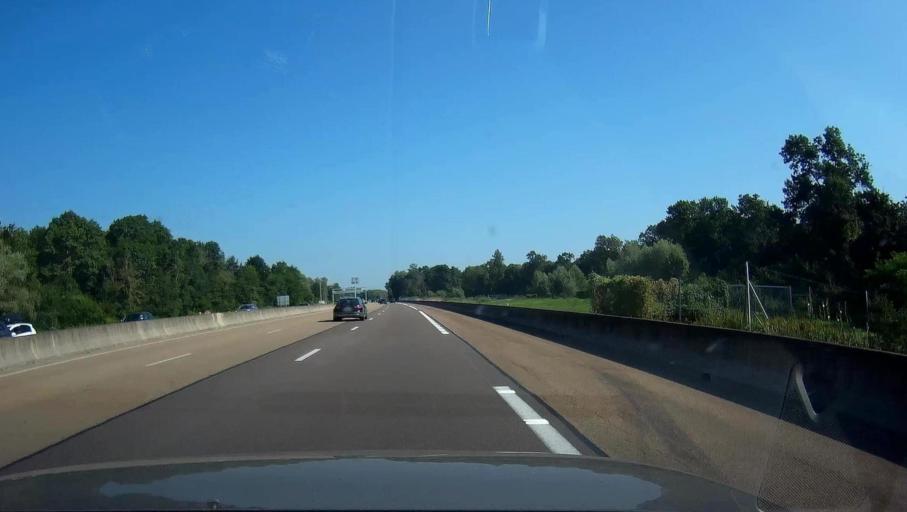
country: FR
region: Bourgogne
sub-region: Departement de la Cote-d'Or
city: Arc-sur-Tille
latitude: 47.3665
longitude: 5.1645
